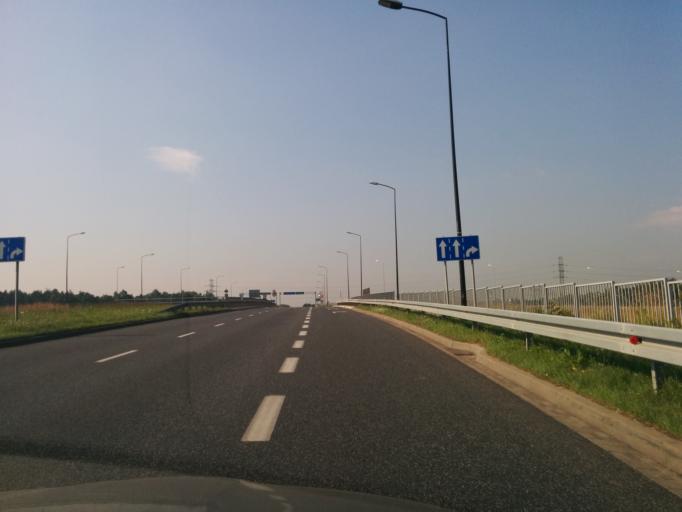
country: PL
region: Silesian Voivodeship
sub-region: Powiat gliwicki
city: Paniowki
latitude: 50.2630
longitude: 18.7980
